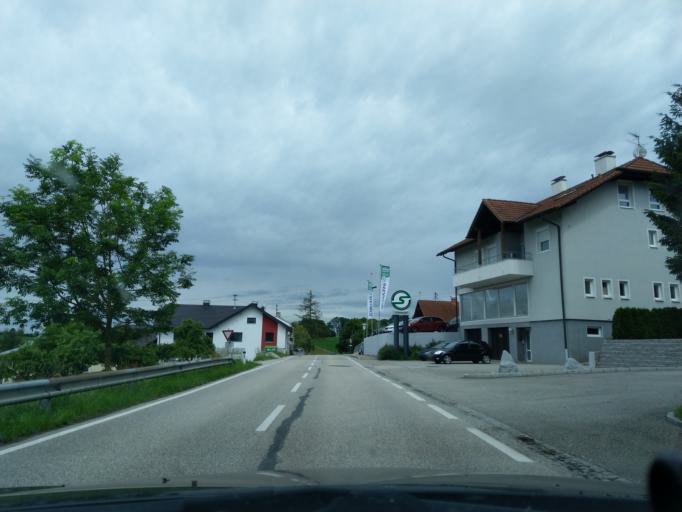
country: DE
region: Bavaria
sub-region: Lower Bavaria
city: Bad Fussing
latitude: 48.2830
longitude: 13.3612
